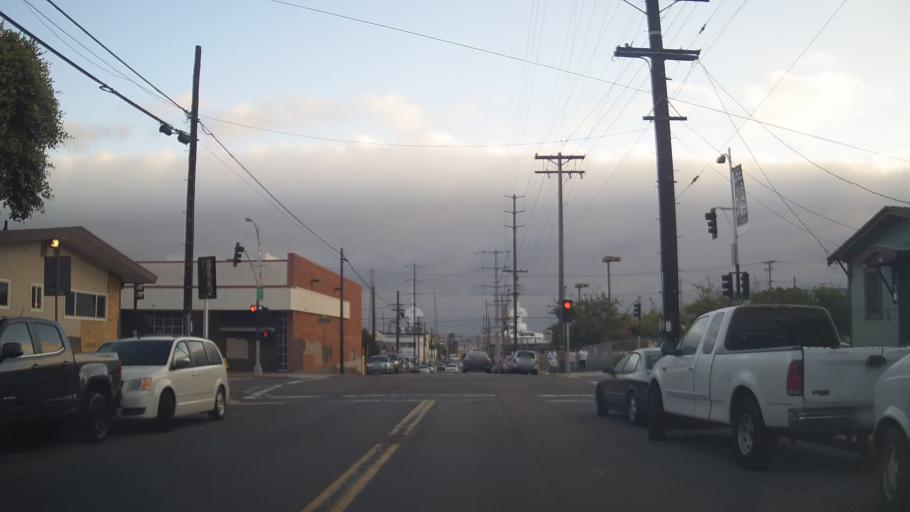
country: US
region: California
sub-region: San Diego County
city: San Diego
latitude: 32.6975
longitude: -117.1399
